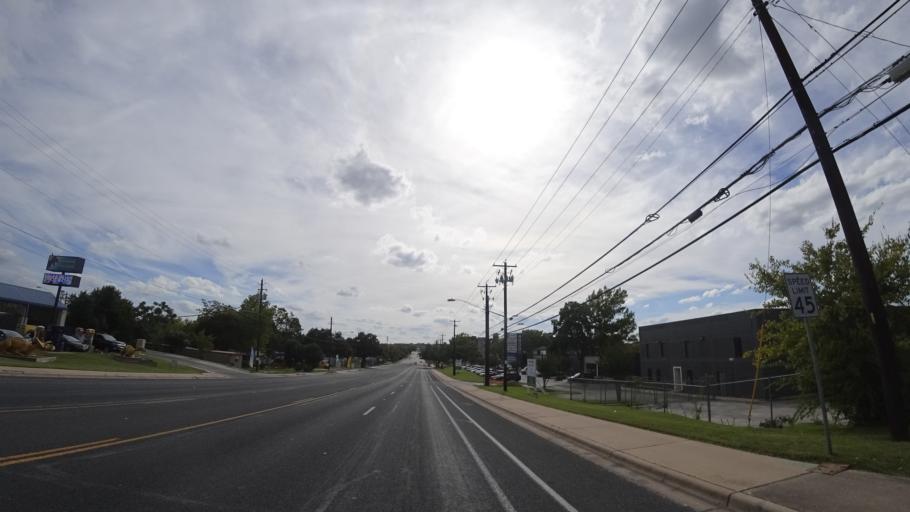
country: US
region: Texas
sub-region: Travis County
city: Austin
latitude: 30.2132
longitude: -97.7701
